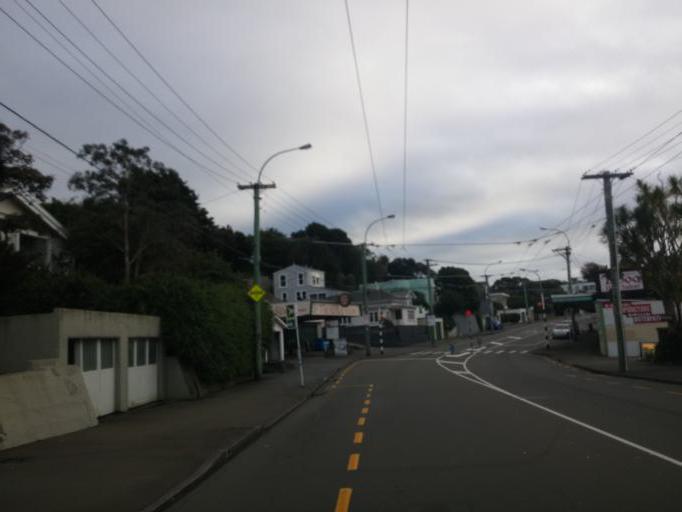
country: NZ
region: Wellington
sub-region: Wellington City
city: Kelburn
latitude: -41.2813
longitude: 174.7506
